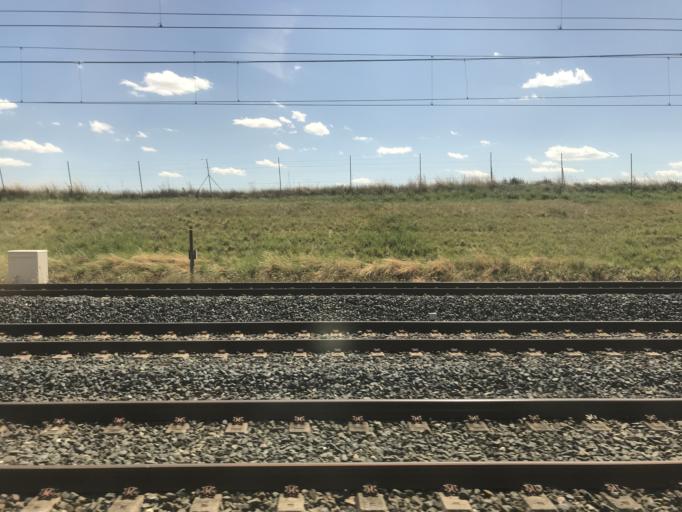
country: FR
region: Lorraine
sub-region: Departement de la Moselle
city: Verny
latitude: 48.9482
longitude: 6.1733
